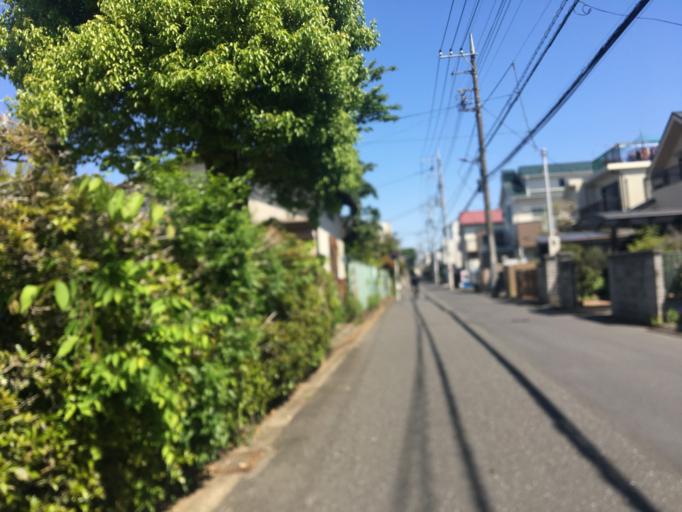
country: JP
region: Tokyo
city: Higashimurayama-shi
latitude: 35.7317
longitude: 139.4864
